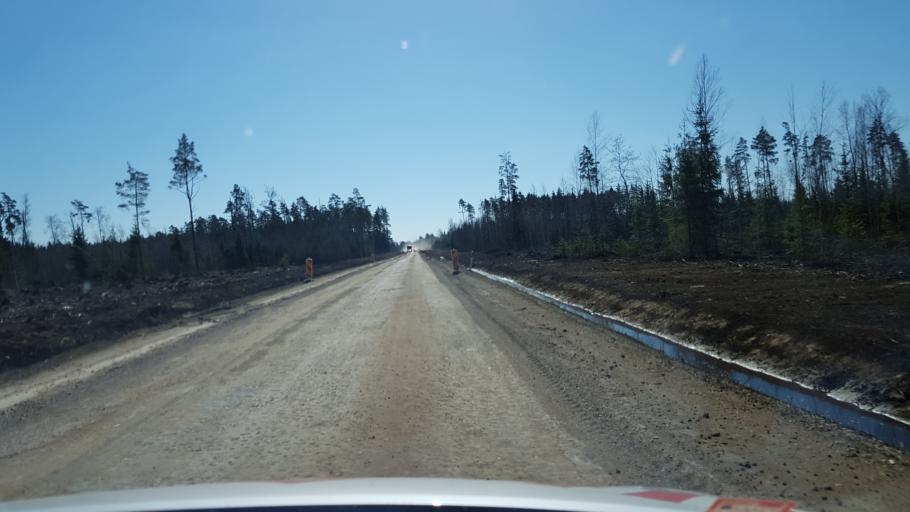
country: EE
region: Laeaene-Virumaa
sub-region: Vinni vald
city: Vinni
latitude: 59.0497
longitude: 26.6565
